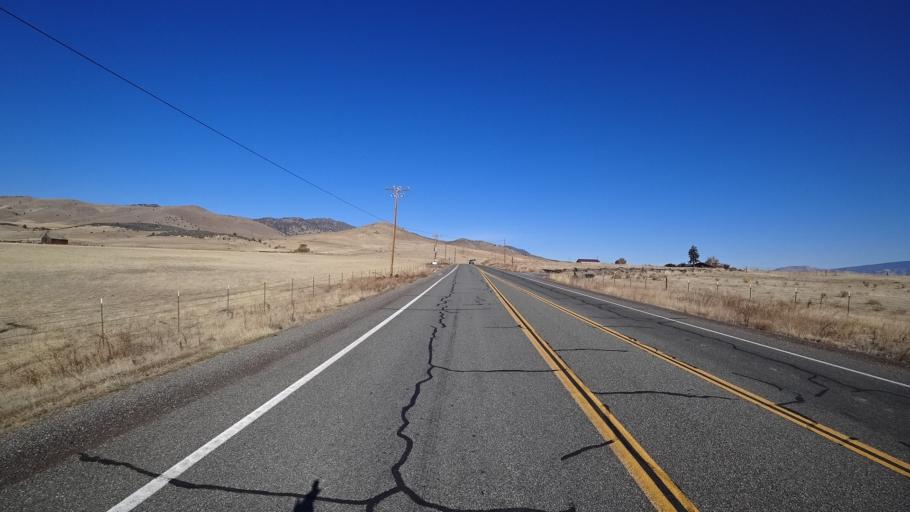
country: US
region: California
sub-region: Siskiyou County
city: Montague
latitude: 41.7721
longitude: -122.5248
